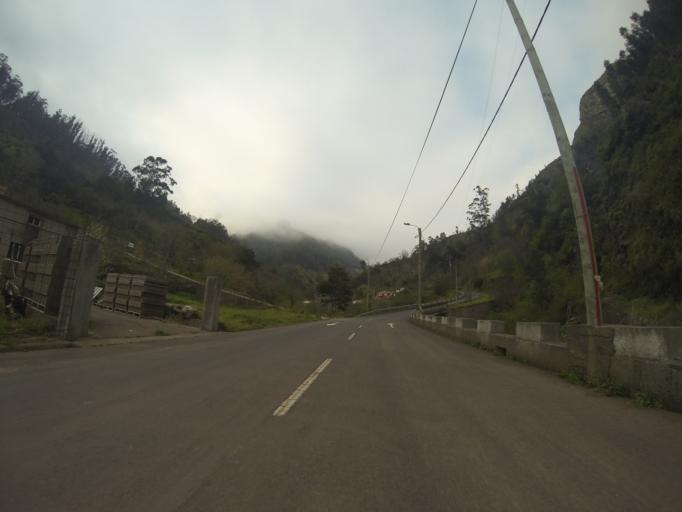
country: PT
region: Madeira
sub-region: Camara de Lobos
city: Curral das Freiras
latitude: 32.7413
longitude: -16.9680
